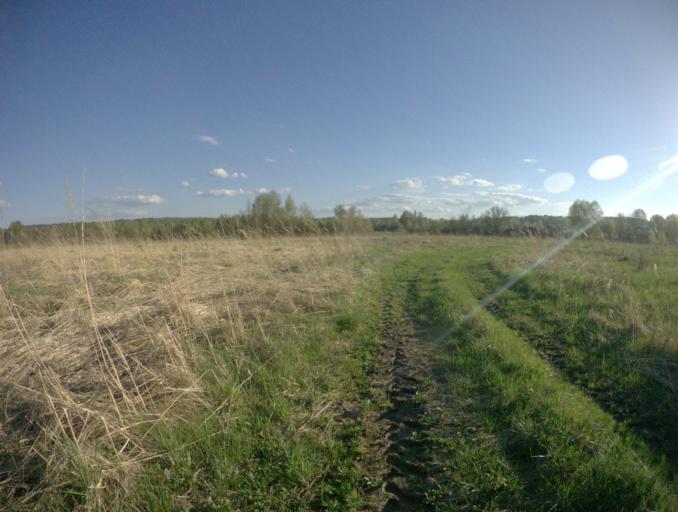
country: RU
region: Vladimir
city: Raduzhnyy
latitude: 56.0070
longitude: 40.2239
